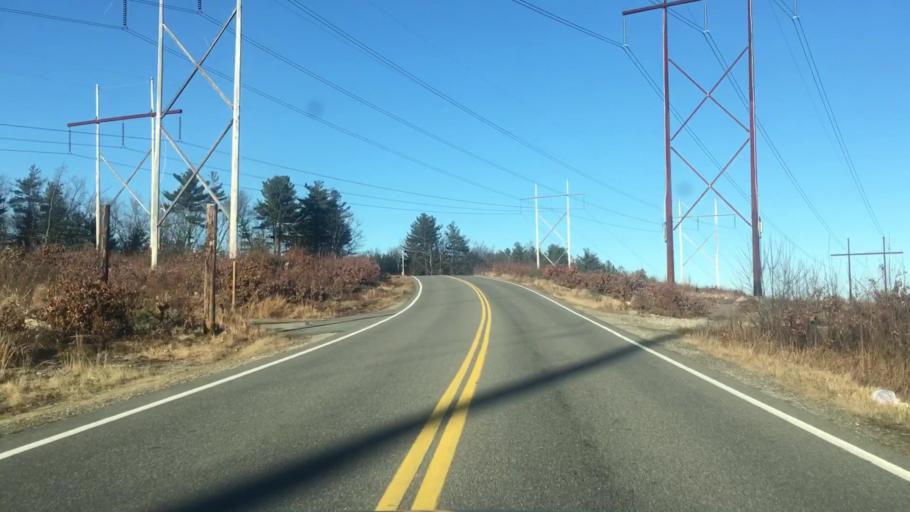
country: US
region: New Hampshire
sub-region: Rockingham County
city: Londonderry
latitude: 42.8889
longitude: -71.3698
